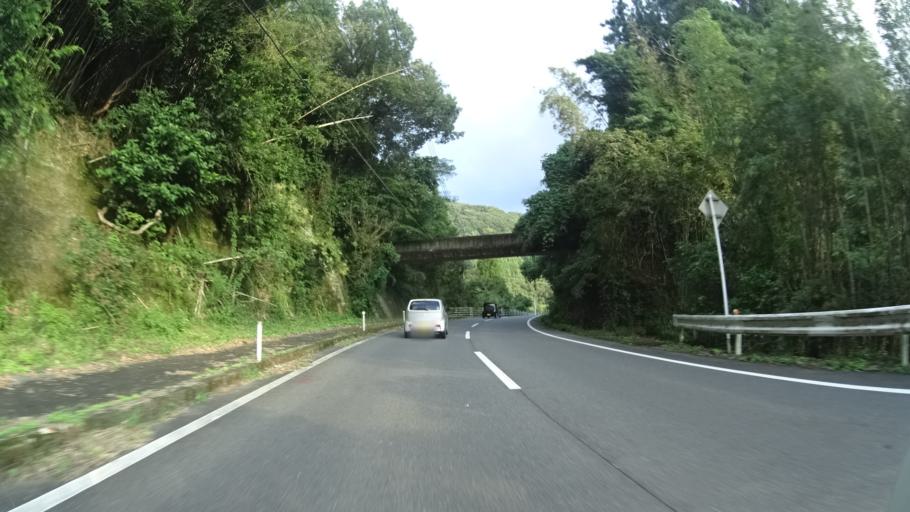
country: JP
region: Oita
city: Hiji
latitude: 33.3697
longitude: 131.3959
